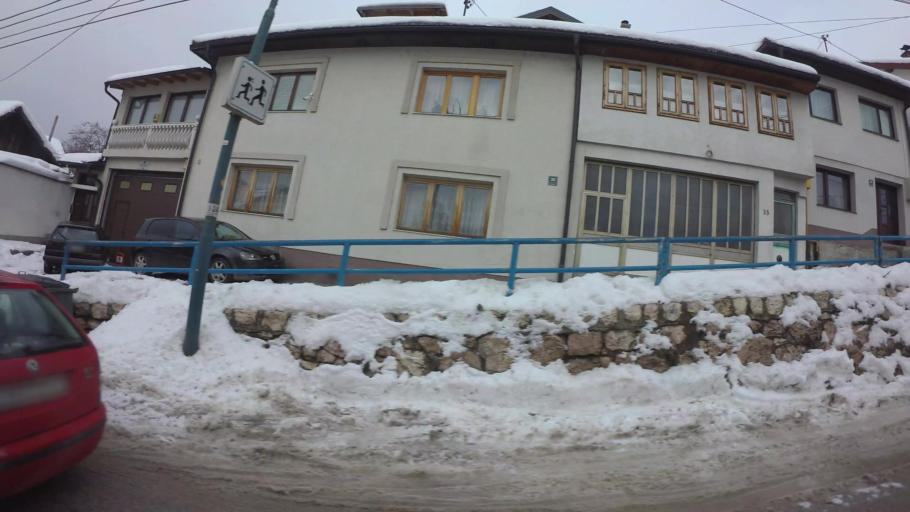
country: BA
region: Federation of Bosnia and Herzegovina
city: Kobilja Glava
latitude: 43.8623
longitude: 18.4443
